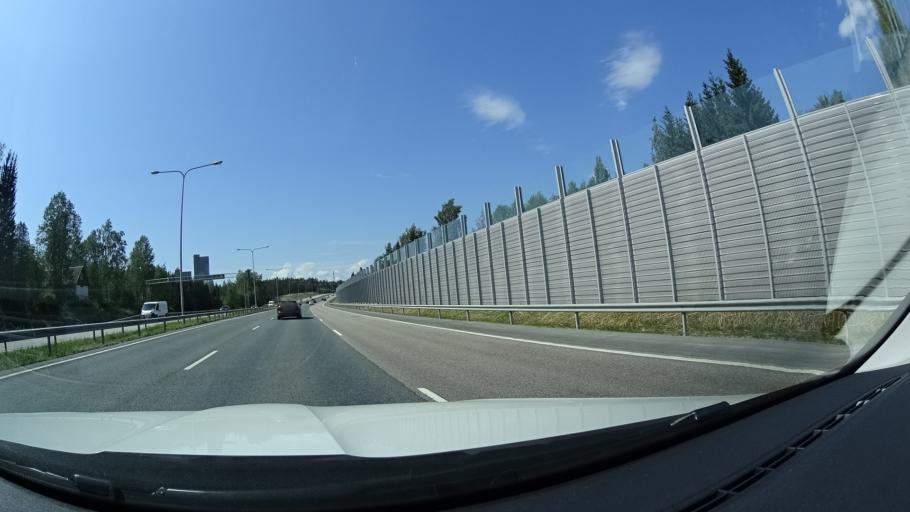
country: FI
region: Uusimaa
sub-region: Helsinki
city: Kauniainen
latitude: 60.2013
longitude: 24.7278
